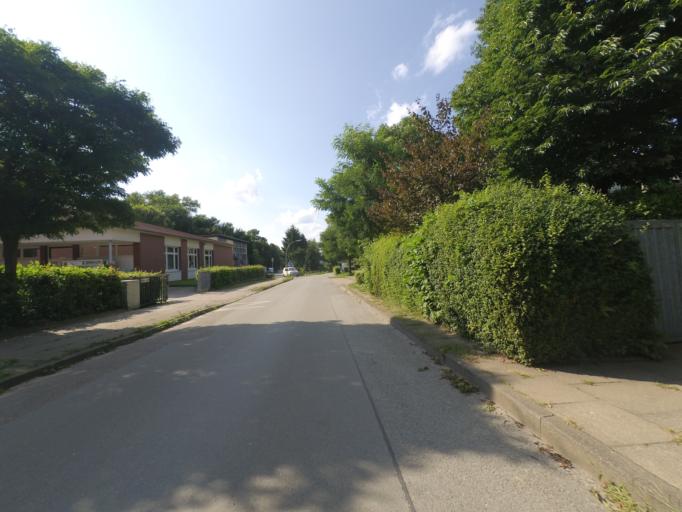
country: DE
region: Schleswig-Holstein
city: Oststeinbek
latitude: 53.5128
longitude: 10.1599
